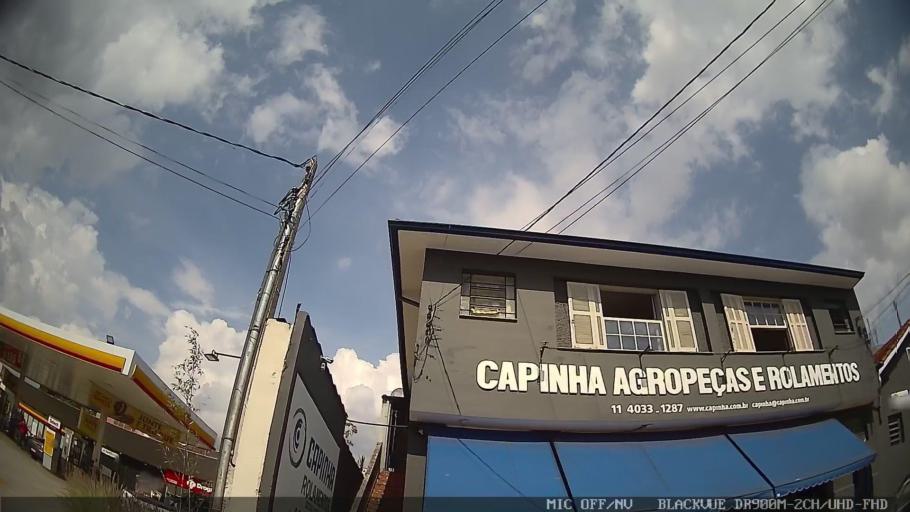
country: BR
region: Sao Paulo
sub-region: Braganca Paulista
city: Braganca Paulista
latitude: -22.9521
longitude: -46.5452
